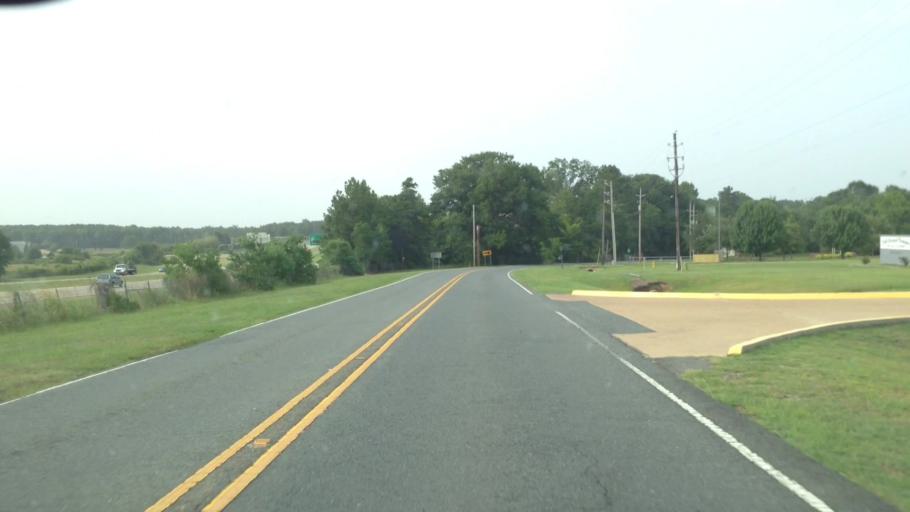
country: US
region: Louisiana
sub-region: Caddo Parish
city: Shreveport
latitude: 32.4474
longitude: -93.8435
